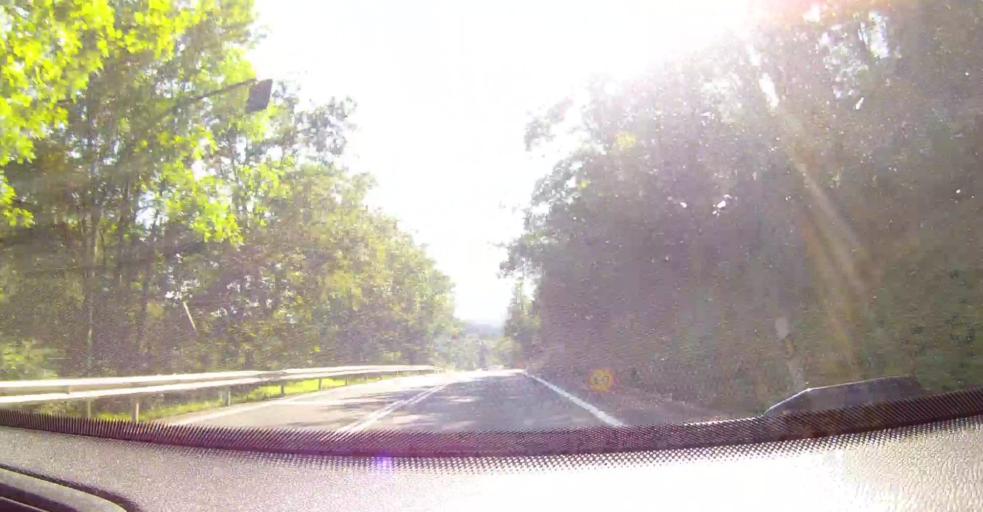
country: ES
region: Basque Country
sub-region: Bizkaia
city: Muxika
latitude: 43.2514
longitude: -2.6945
